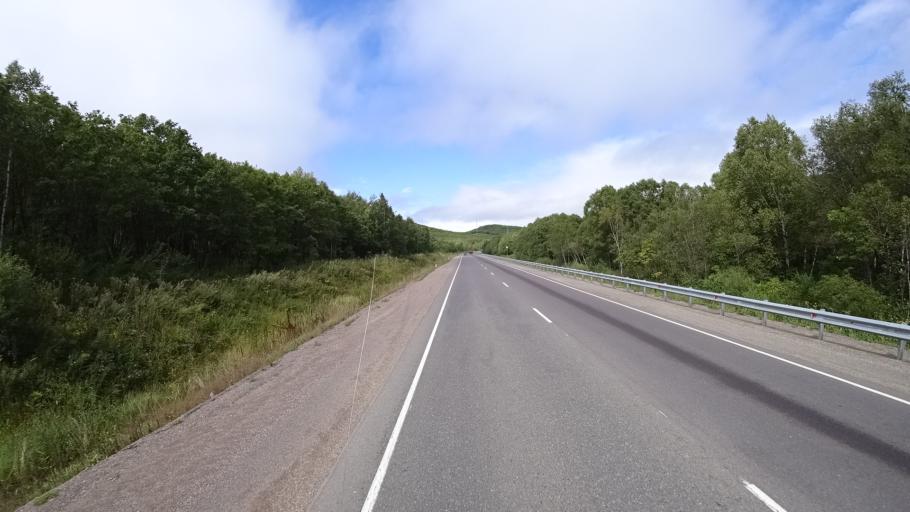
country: RU
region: Primorskiy
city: Lyalichi
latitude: 44.1134
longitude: 132.4196
